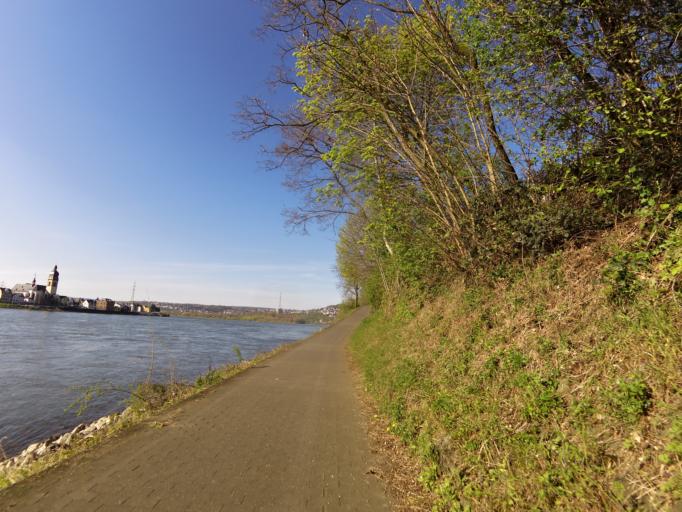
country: DE
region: Rheinland-Pfalz
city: Urbar
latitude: 50.3731
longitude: 7.6142
